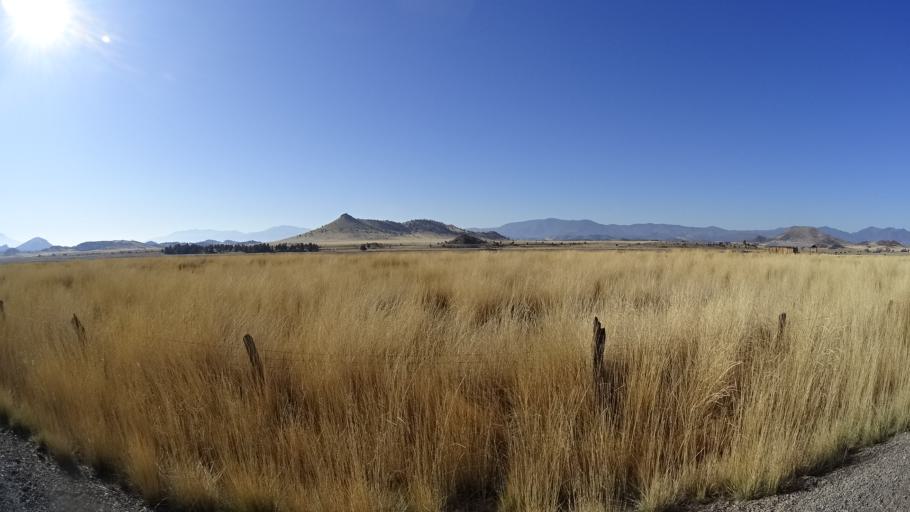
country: US
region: California
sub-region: Siskiyou County
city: Montague
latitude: 41.7205
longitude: -122.4532
